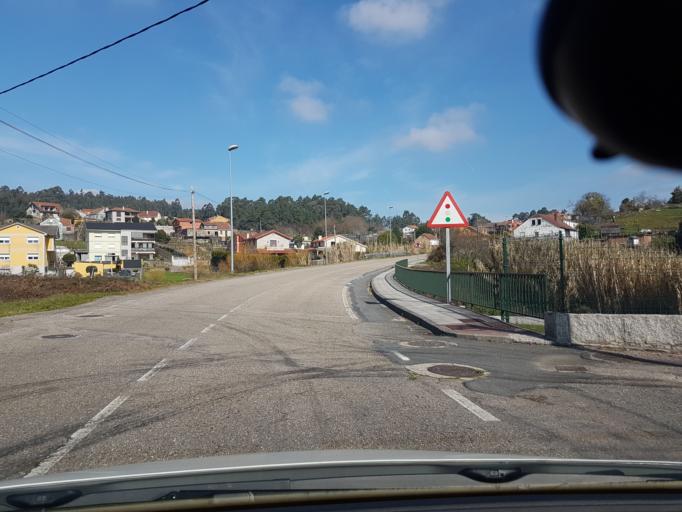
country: ES
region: Galicia
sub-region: Provincia de Pontevedra
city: Porrino
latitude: 42.1999
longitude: -8.6487
